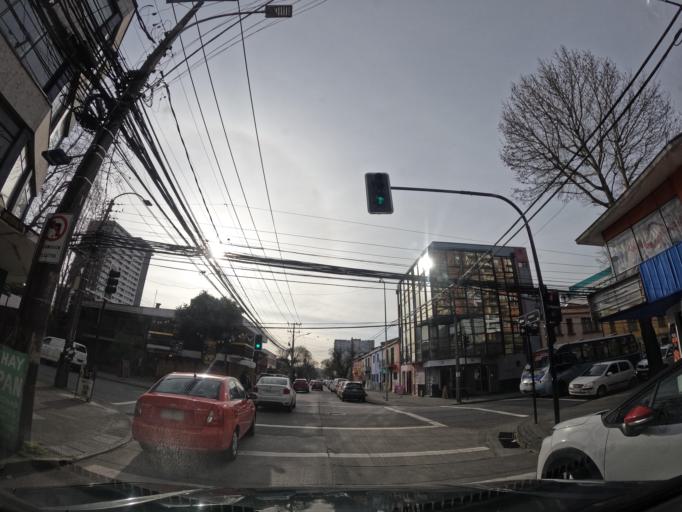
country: CL
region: Biobio
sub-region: Provincia de Concepcion
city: Concepcion
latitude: -36.8217
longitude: -73.0416
